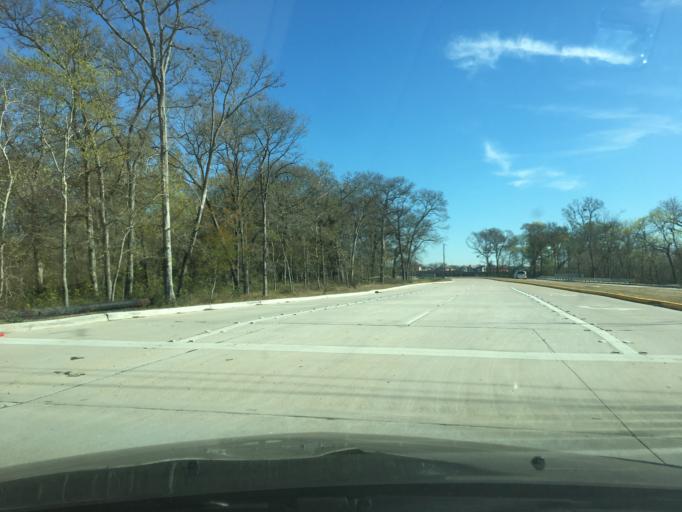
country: US
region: Texas
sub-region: Fort Bend County
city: Greatwood
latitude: 29.5522
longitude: -95.7189
